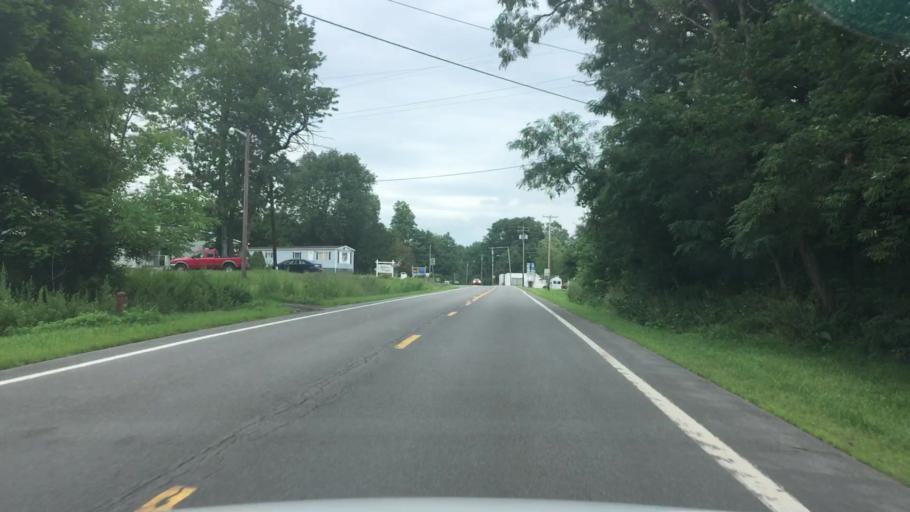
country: US
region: New York
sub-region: Otsego County
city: West End
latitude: 42.4392
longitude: -75.1132
